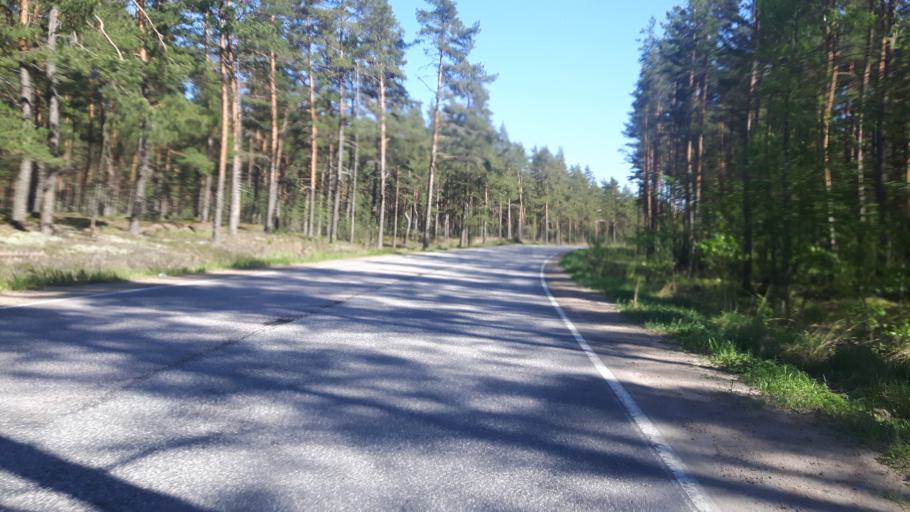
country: RU
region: Leningrad
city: Glebychevo
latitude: 60.2761
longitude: 28.9267
